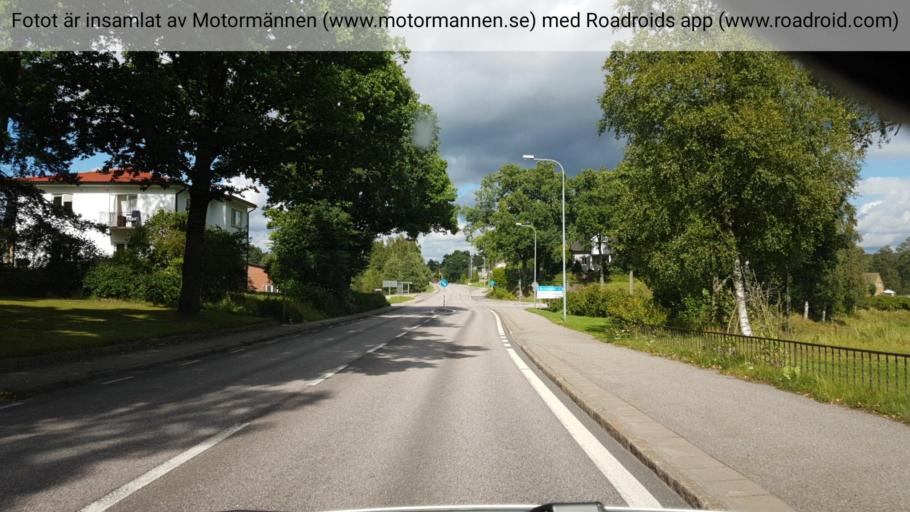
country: SE
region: Vaestra Goetaland
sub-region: Ulricehamns Kommun
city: Ulricehamn
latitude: 57.8997
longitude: 13.4680
